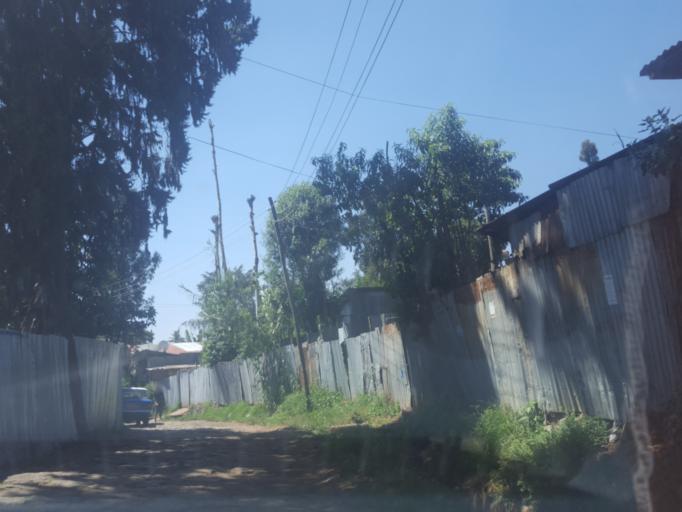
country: ET
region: Adis Abeba
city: Addis Ababa
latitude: 9.0630
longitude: 38.7409
